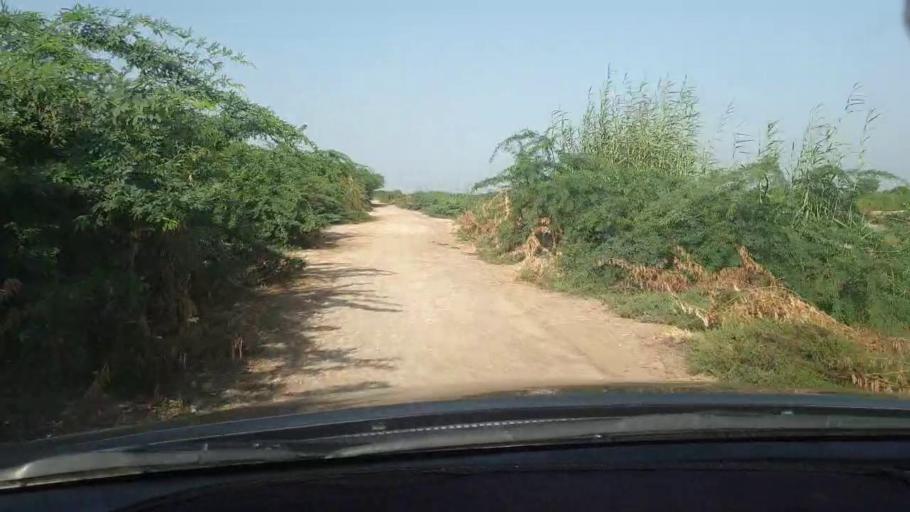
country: PK
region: Sindh
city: Tando Bago
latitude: 24.6741
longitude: 69.1838
